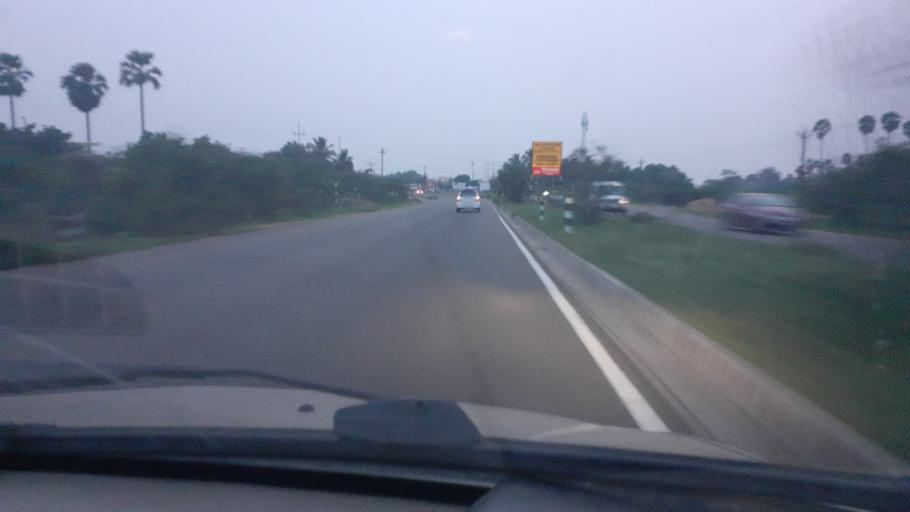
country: IN
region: Tamil Nadu
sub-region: Thoothukkudi
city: Srivaikuntam
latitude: 8.7117
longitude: 77.8254
